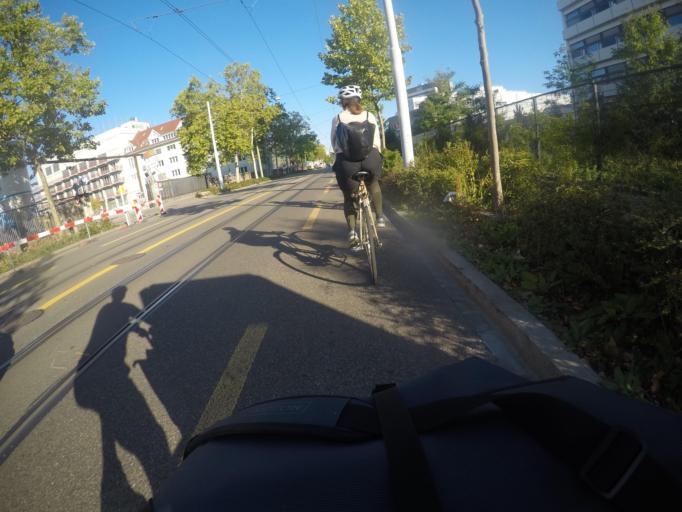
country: CH
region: Basel-City
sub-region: Basel-Stadt
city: Basel
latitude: 47.5733
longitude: 7.5757
